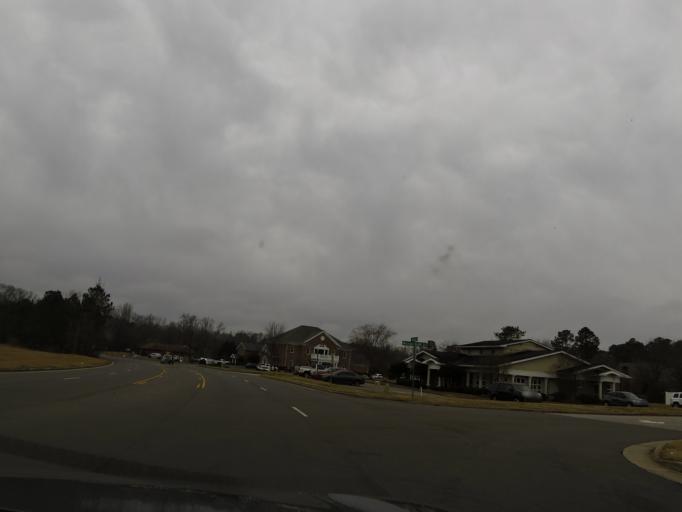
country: US
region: North Carolina
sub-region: Nash County
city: Rocky Mount
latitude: 35.9450
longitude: -77.8494
